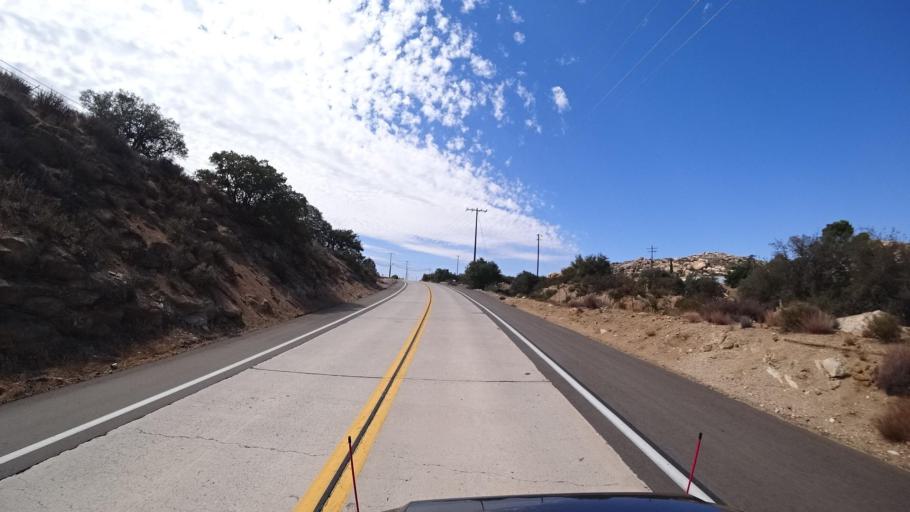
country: MX
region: Baja California
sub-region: Tecate
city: Cereso del Hongo
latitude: 32.6431
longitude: -116.2317
